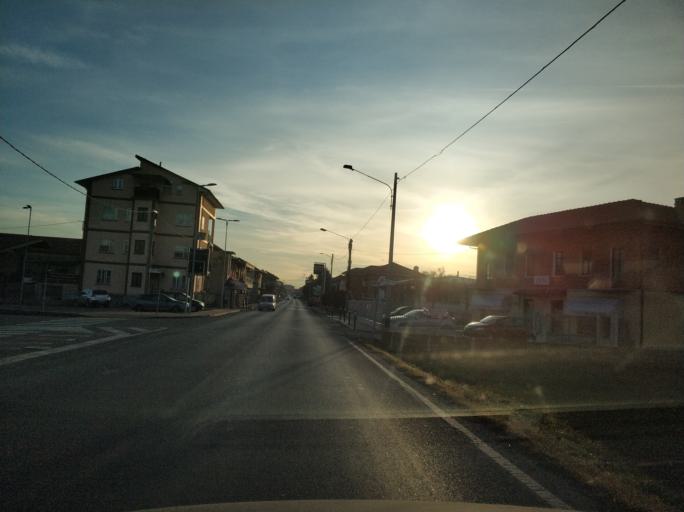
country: IT
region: Piedmont
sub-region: Provincia di Torino
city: San Maurizio
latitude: 45.2241
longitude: 7.6397
